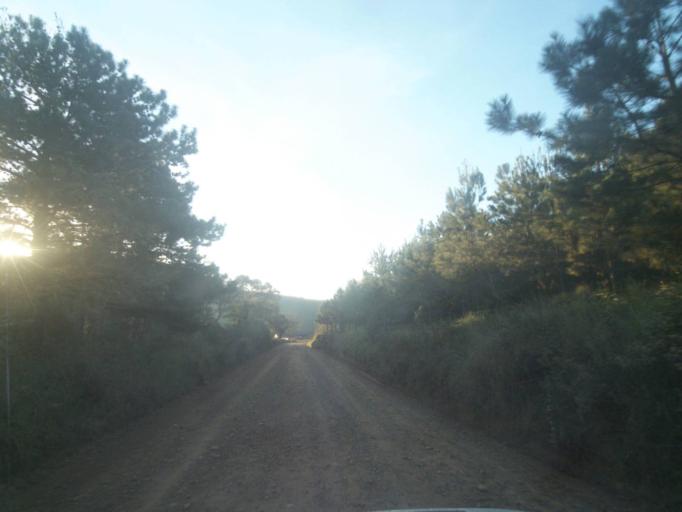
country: BR
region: Parana
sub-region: Tibagi
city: Tibagi
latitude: -24.5399
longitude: -50.5323
